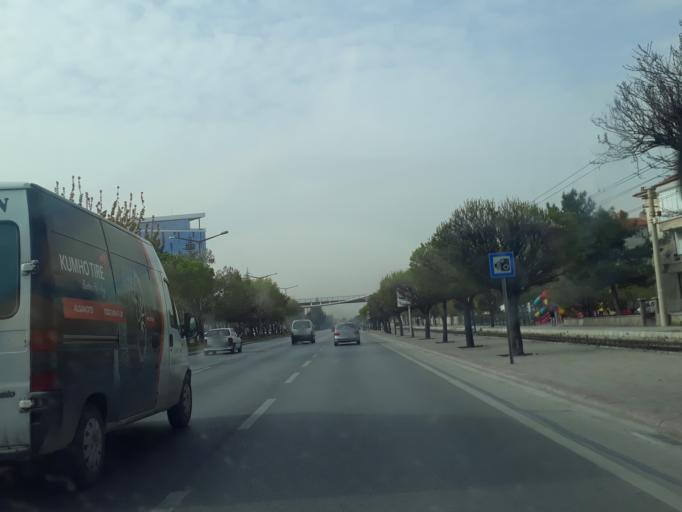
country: TR
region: Konya
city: Selcuklu
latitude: 37.9391
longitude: 32.5113
